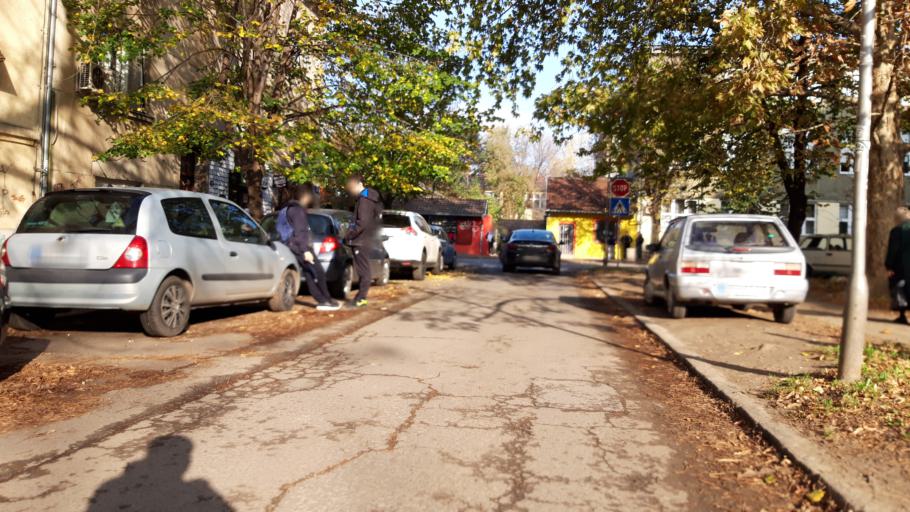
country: RS
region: Autonomna Pokrajina Vojvodina
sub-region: Juznobacki Okrug
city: Novi Sad
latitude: 45.2589
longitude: 19.8523
